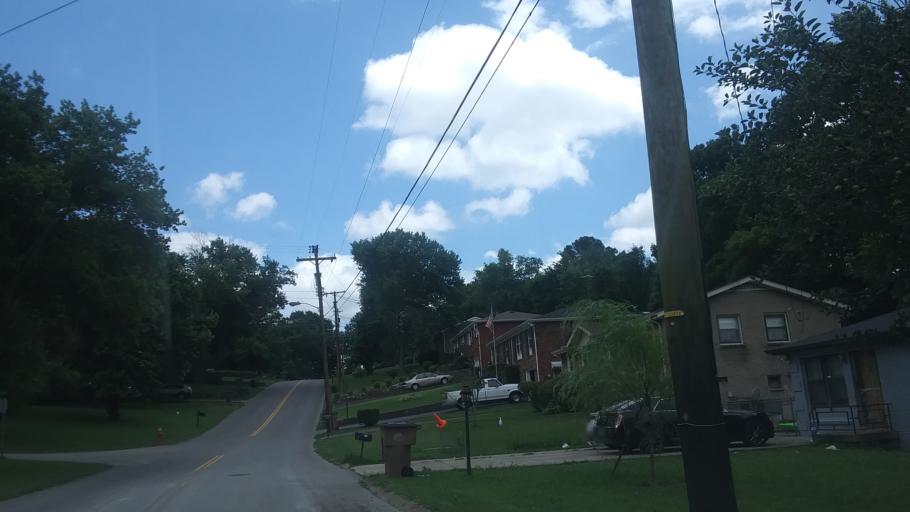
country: US
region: Tennessee
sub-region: Davidson County
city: Oak Hill
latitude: 36.0854
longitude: -86.7131
